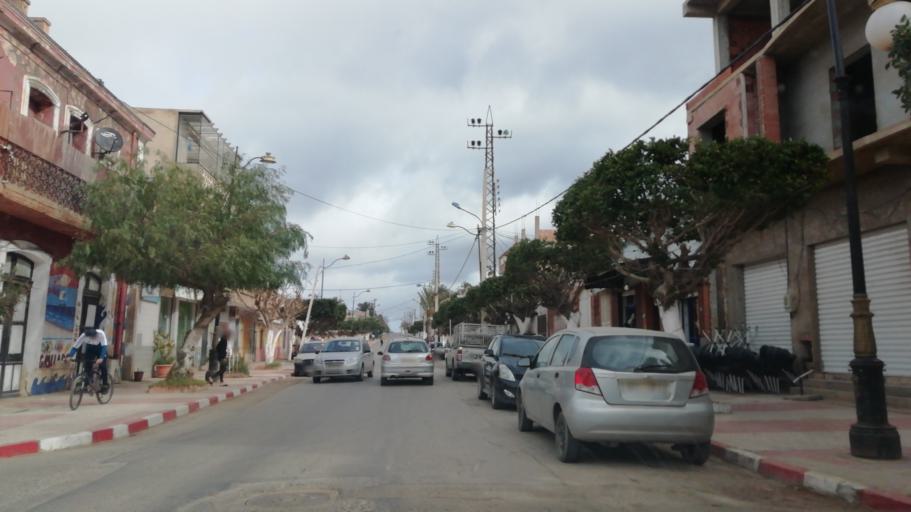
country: DZ
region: Oran
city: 'Ain el Turk
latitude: 35.6867
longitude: -0.8686
